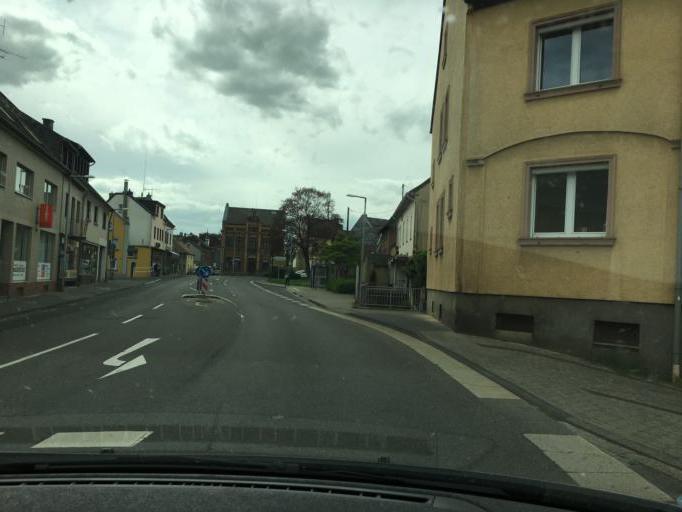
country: DE
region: North Rhine-Westphalia
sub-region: Regierungsbezirk Koln
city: Euskirchen
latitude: 50.6506
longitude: 6.8280
